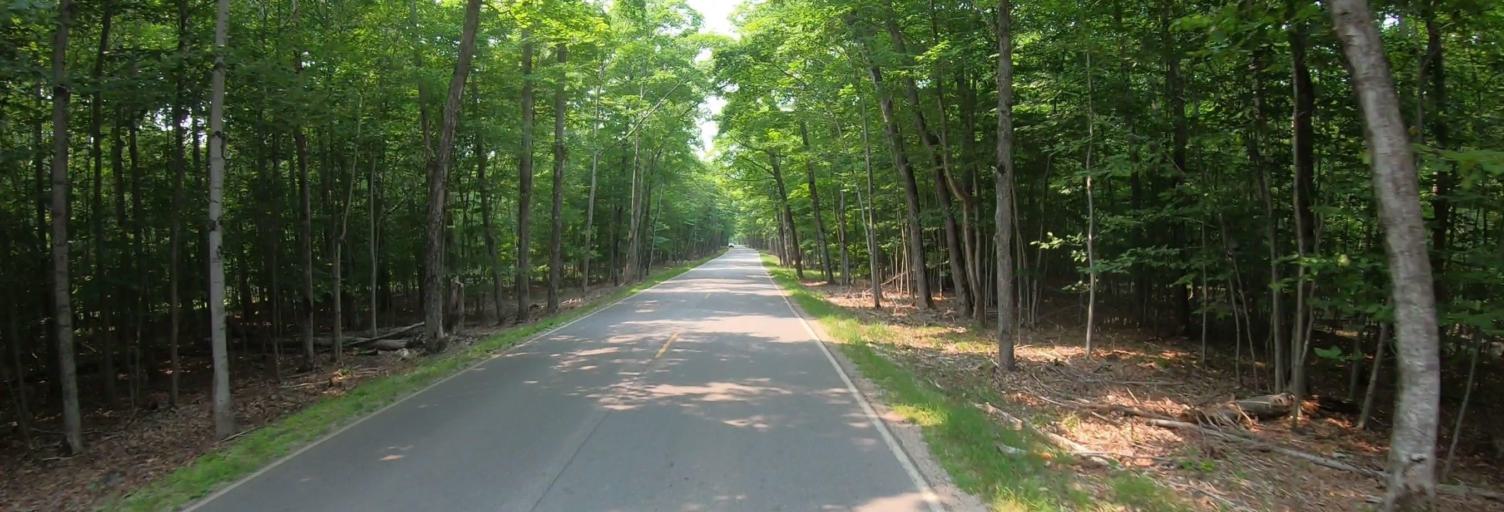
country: CA
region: Ontario
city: Thessalon
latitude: 46.0131
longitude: -83.6981
